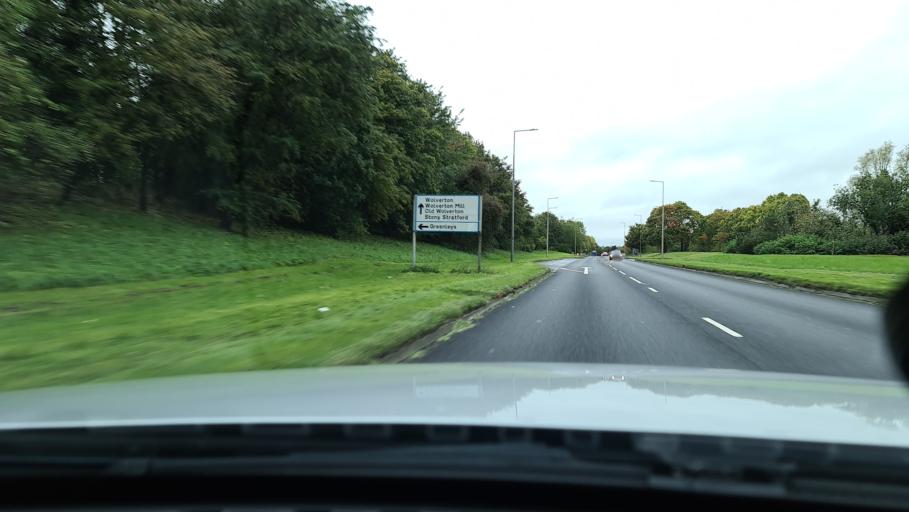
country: GB
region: England
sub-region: Milton Keynes
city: Stony Stratford
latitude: 52.0554
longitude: -0.8207
